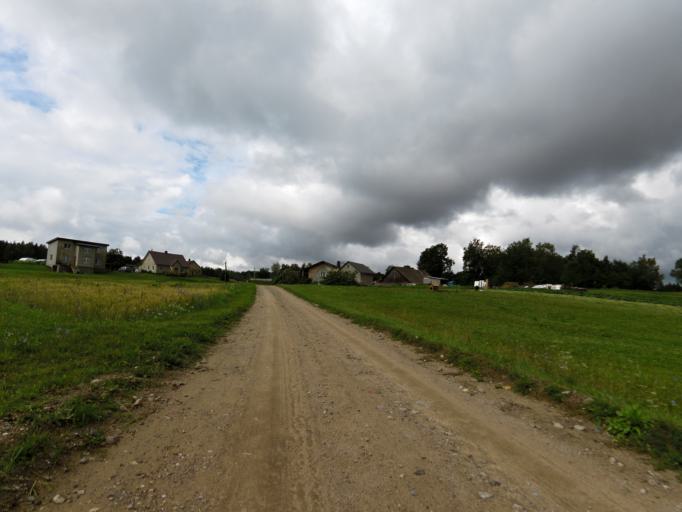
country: LT
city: Grigiskes
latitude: 54.7030
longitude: 25.1134
